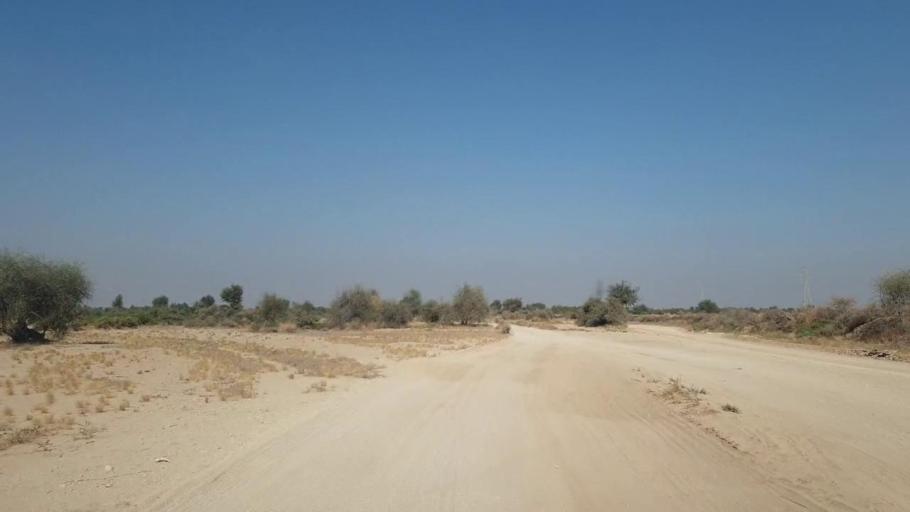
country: PK
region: Sindh
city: Jamshoro
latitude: 25.2850
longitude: 67.8115
